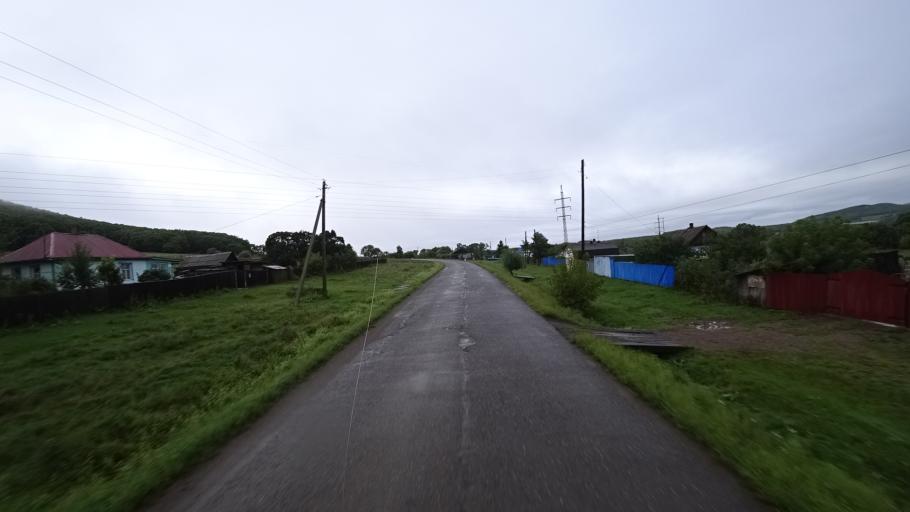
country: RU
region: Primorskiy
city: Monastyrishche
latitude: 44.2615
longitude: 132.4200
